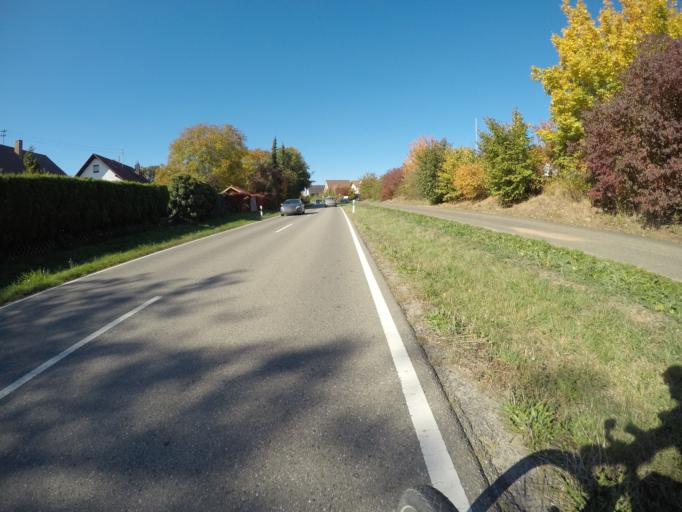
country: DE
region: Baden-Wuerttemberg
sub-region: Regierungsbezirk Stuttgart
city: Bondorf
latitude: 48.5523
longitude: 8.8327
